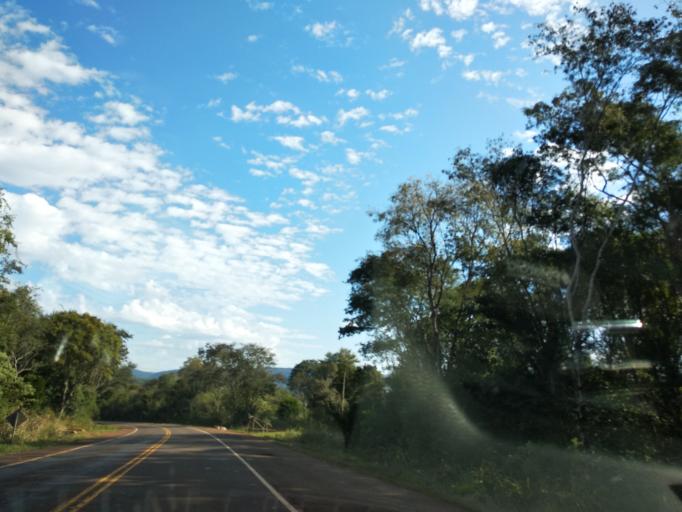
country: AR
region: Misiones
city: Aristobulo del Valle
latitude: -27.0989
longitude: -54.9594
